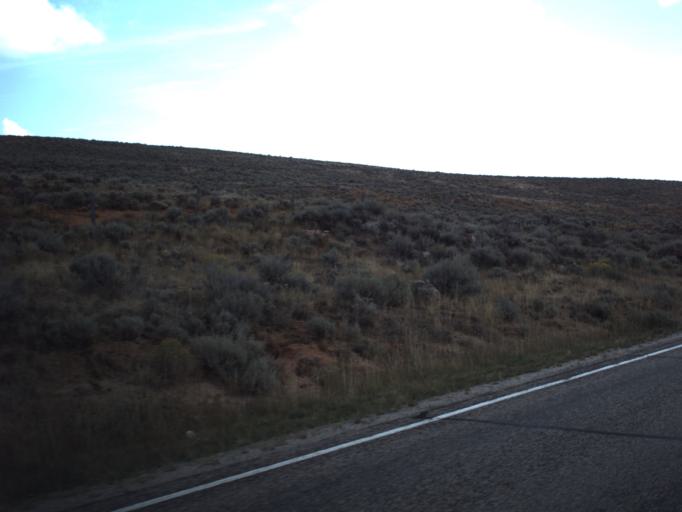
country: US
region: Utah
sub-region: Rich County
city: Randolph
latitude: 41.7930
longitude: -111.2213
